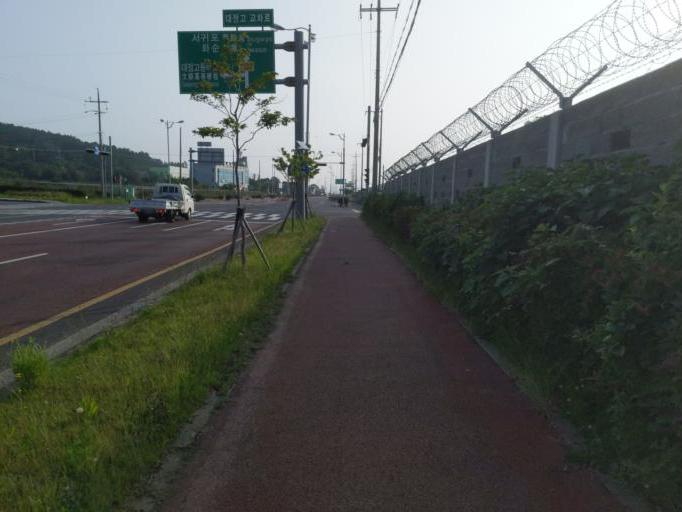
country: KR
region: Jeju-do
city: Gaigeturi
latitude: 33.2303
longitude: 126.2620
